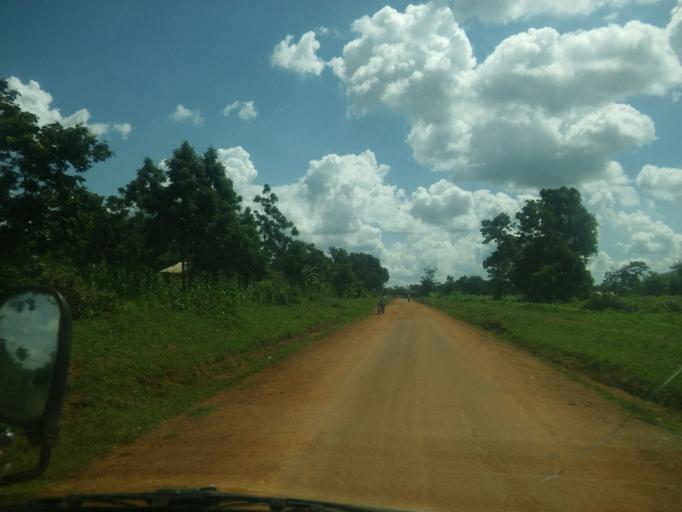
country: UG
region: Eastern Region
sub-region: Pallisa District
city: Pallisa
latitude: 1.1512
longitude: 33.8104
